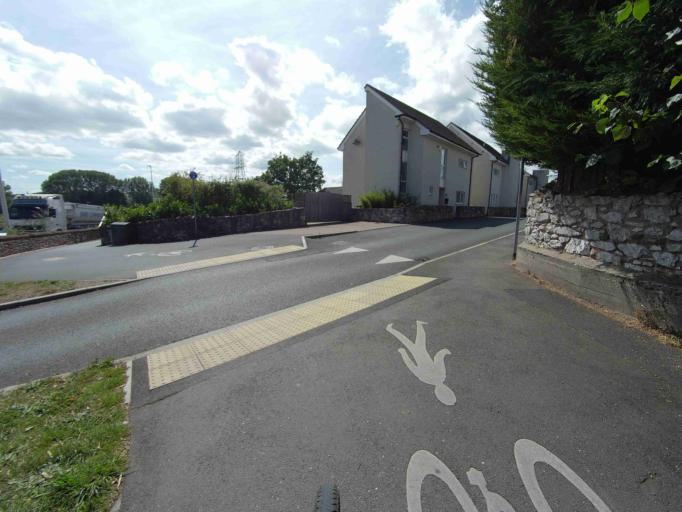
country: GB
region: England
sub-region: Devon
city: Exminster
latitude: 50.6970
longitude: -3.4979
